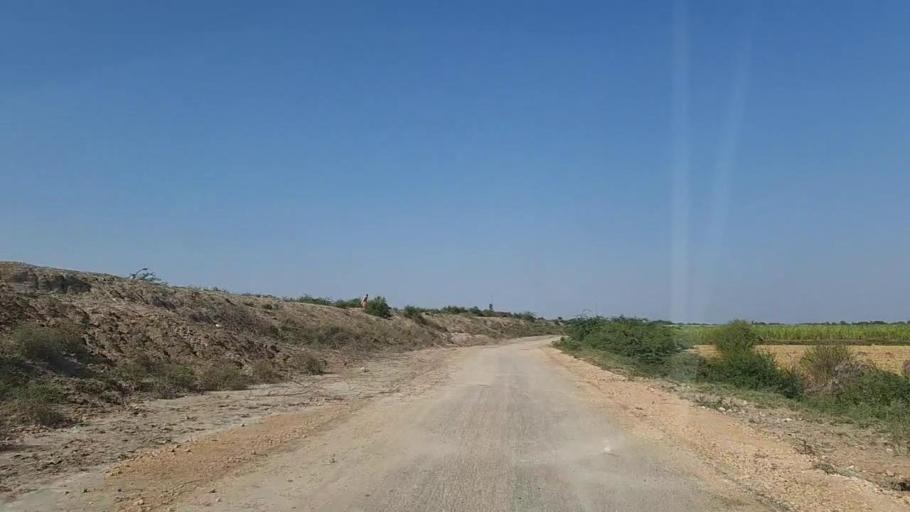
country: PK
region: Sindh
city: Chuhar Jamali
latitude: 24.5750
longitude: 68.0297
